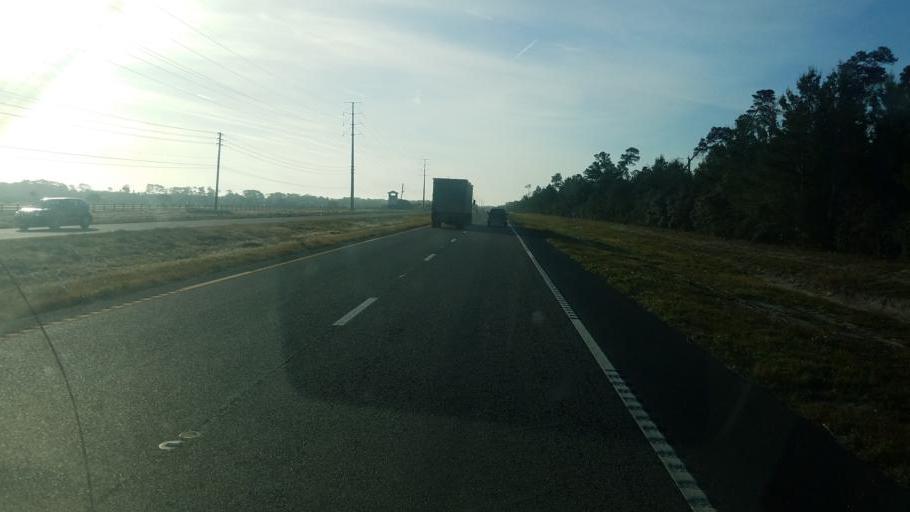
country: US
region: Florida
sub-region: Osceola County
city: Saint Cloud
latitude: 28.2168
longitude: -81.1773
